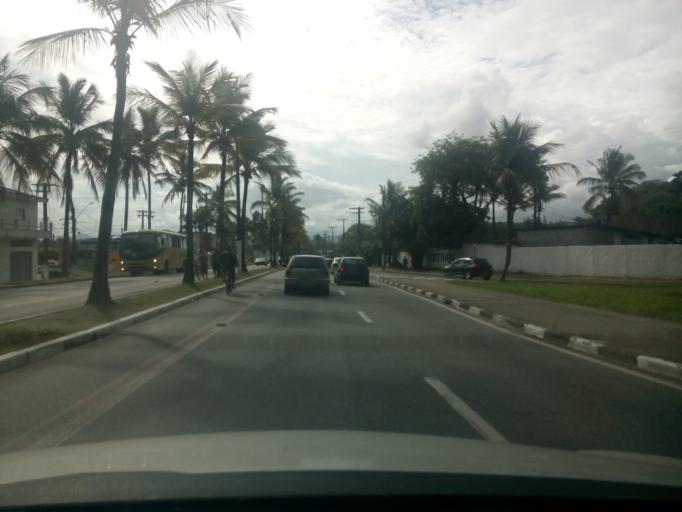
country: BR
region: Sao Paulo
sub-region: Guaruja
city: Guaruja
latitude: -23.9887
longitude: -46.2613
